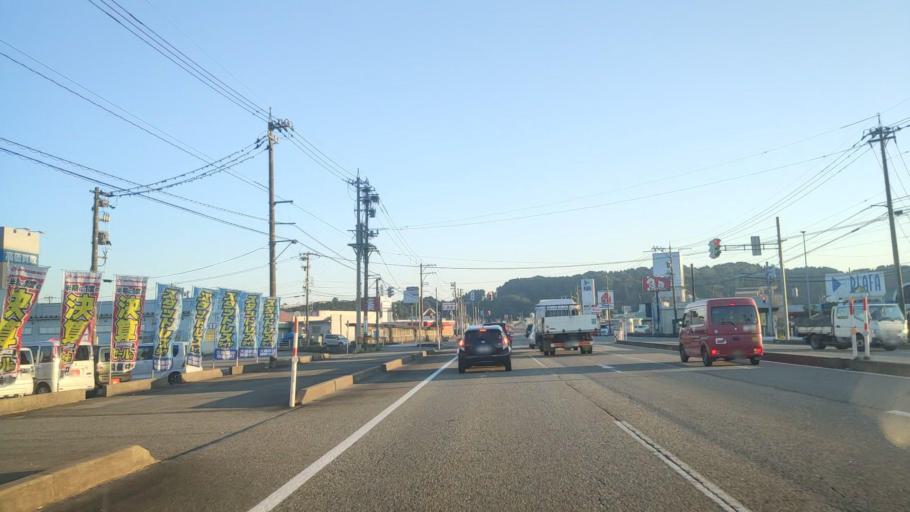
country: JP
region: Toyama
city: Himi
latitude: 36.8646
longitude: 136.9756
